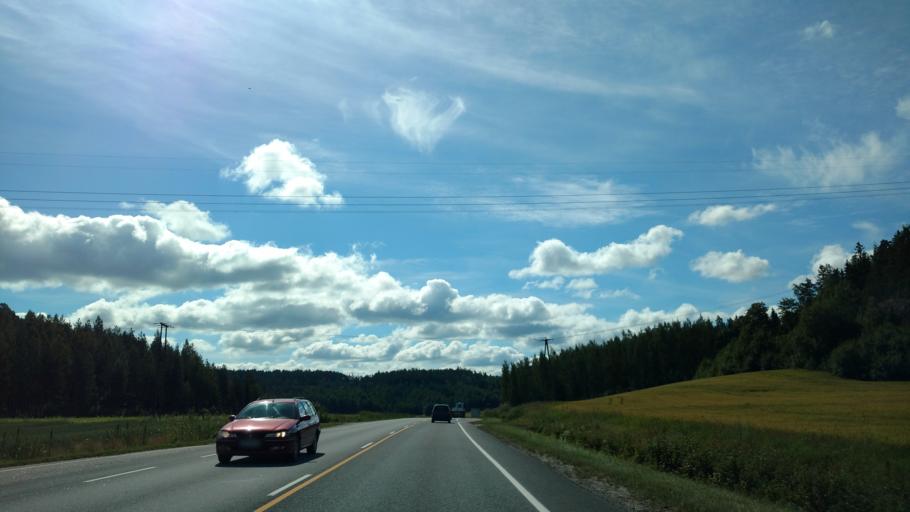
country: FI
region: Varsinais-Suomi
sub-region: Salo
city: Salo
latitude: 60.3647
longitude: 23.1401
